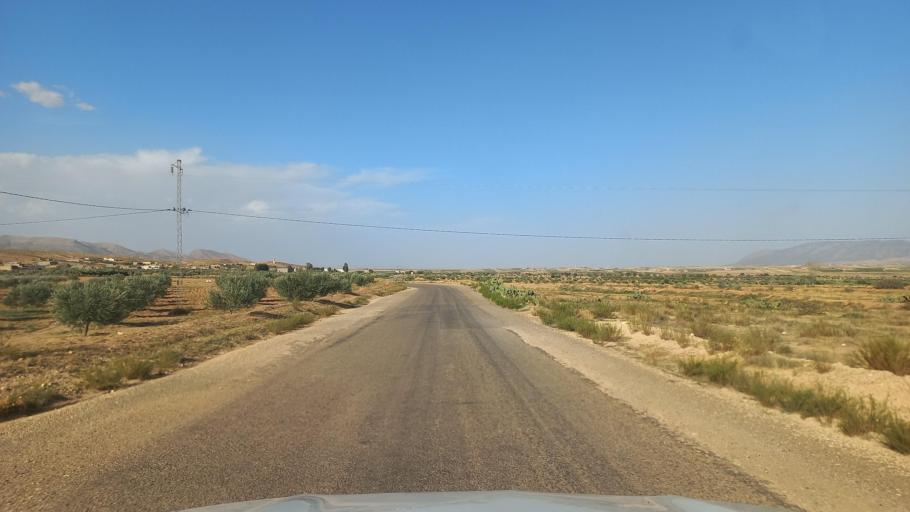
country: TN
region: Al Qasrayn
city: Sbiba
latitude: 35.3692
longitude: 9.0100
